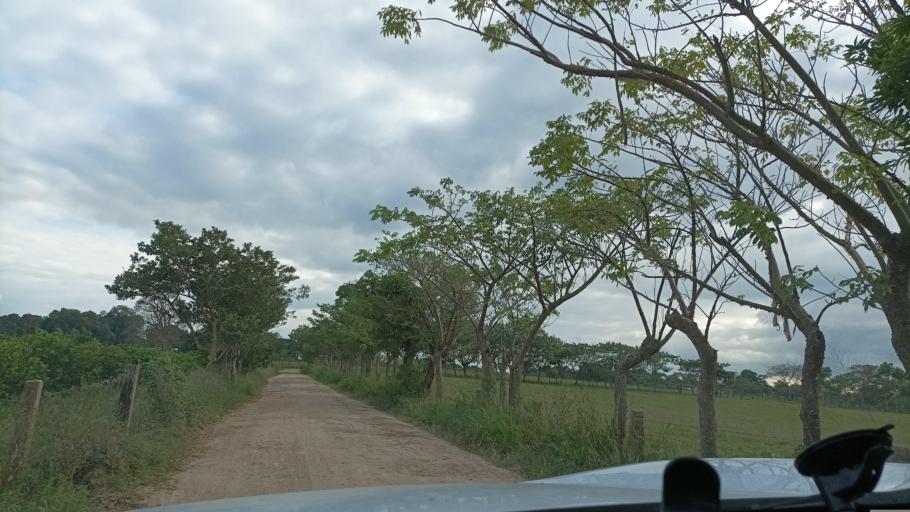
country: MX
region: Veracruz
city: Oluta
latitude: 17.9296
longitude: -94.8839
